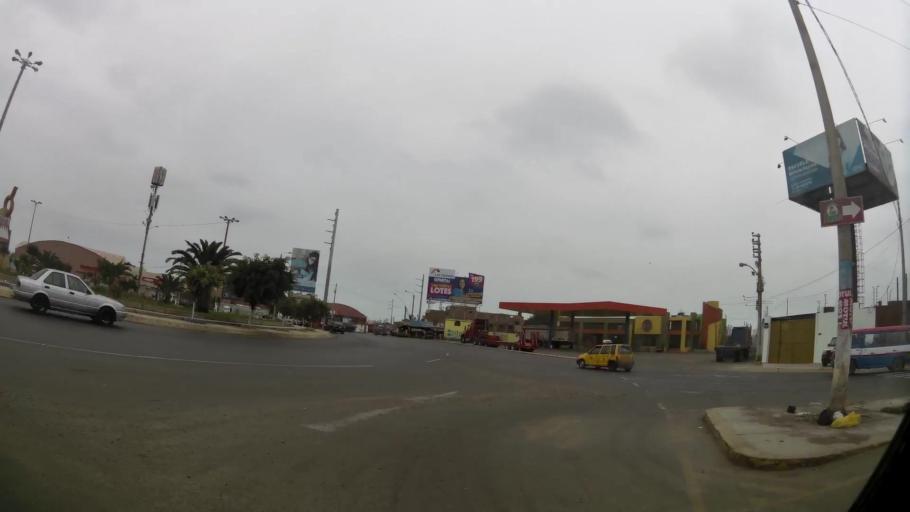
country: PE
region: La Libertad
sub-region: Provincia de Trujillo
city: Trujillo
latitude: -8.1302
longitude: -79.0212
